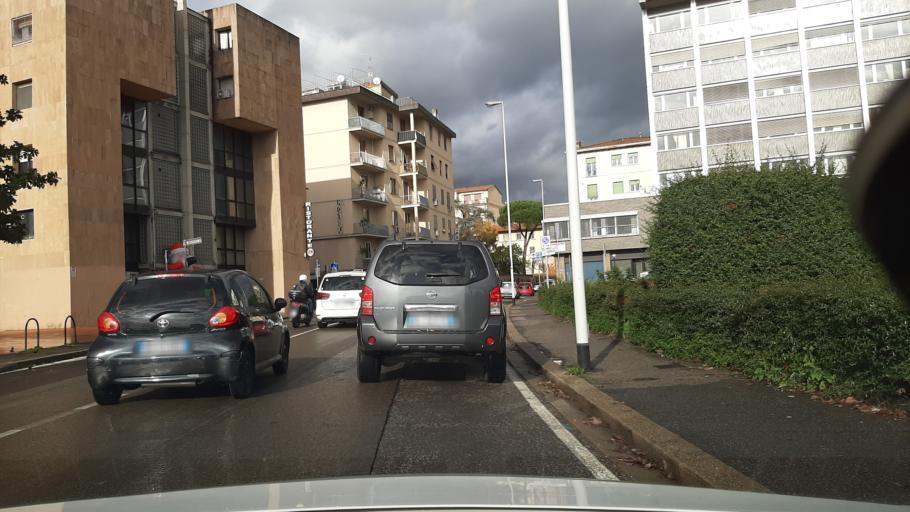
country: IT
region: Tuscany
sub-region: Province of Florence
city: Florence
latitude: 43.7964
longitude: 11.2448
